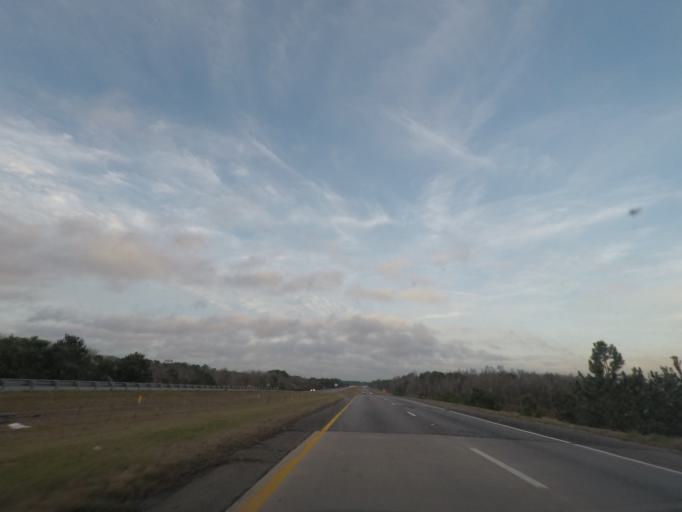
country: US
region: South Carolina
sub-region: Orangeburg County
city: Holly Hill
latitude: 33.3828
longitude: -80.5187
